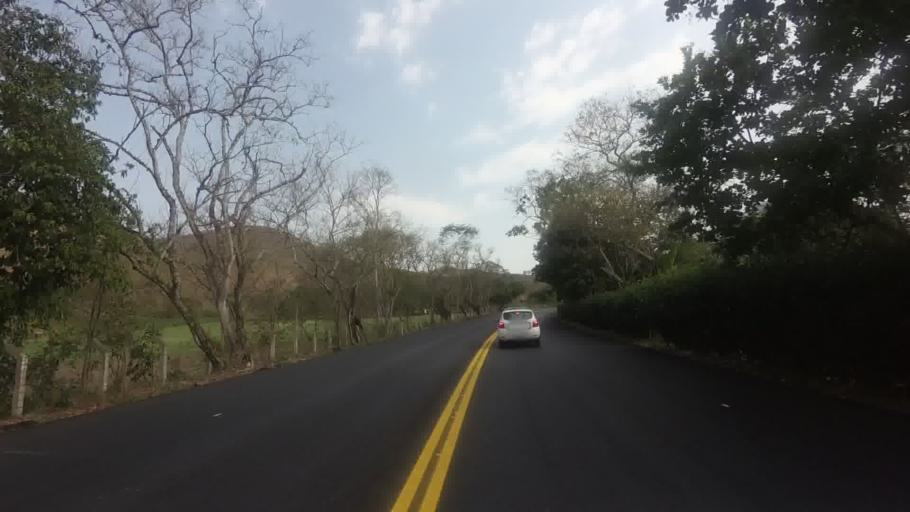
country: BR
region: Rio de Janeiro
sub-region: Bom Jesus Do Itabapoana
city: Bom Jesus do Itabapoana
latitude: -21.2204
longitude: -41.7387
